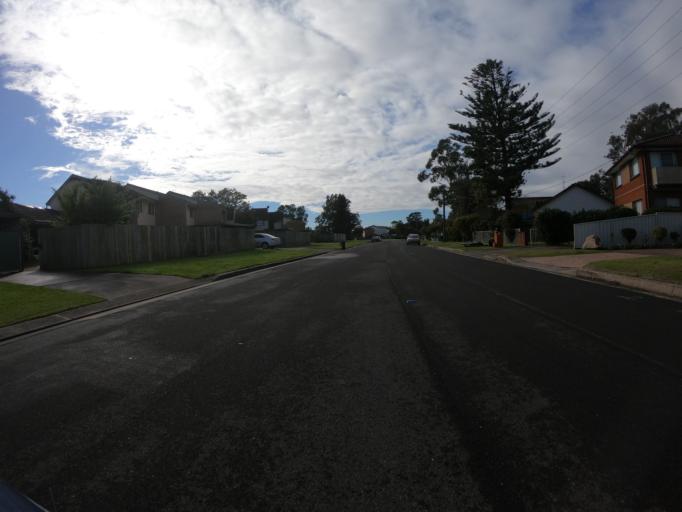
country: AU
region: New South Wales
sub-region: Wollongong
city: East Corrimal
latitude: -34.3721
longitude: 150.9166
